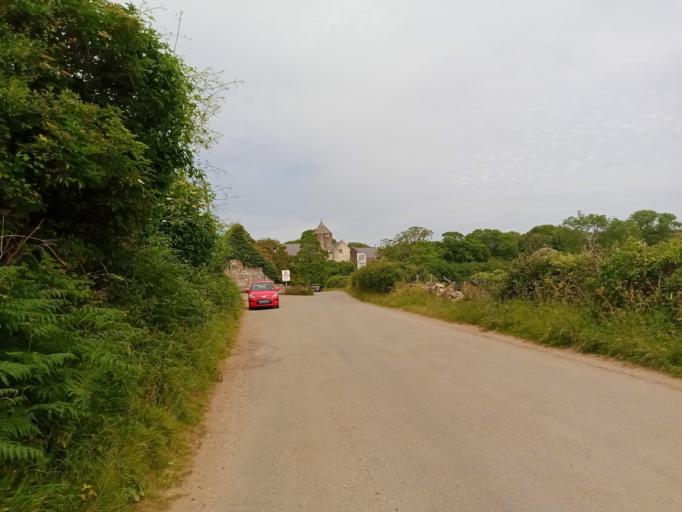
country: GB
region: Wales
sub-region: Anglesey
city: Llangoed
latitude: 53.3044
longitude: -4.0578
